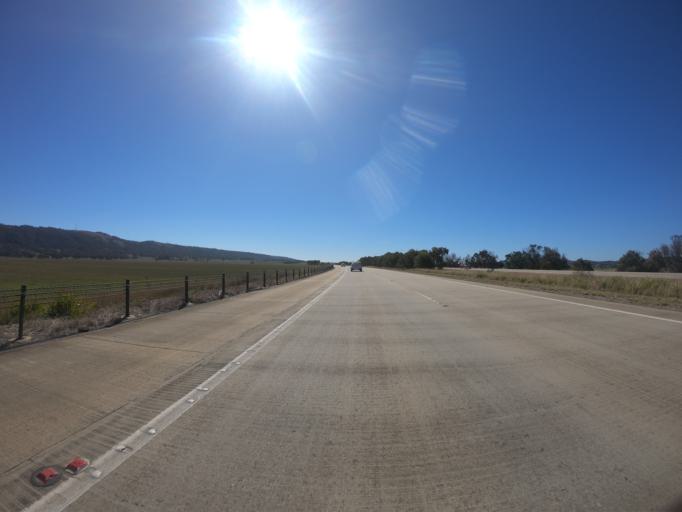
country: AU
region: New South Wales
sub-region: Yass Valley
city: Gundaroo
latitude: -34.9602
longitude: 149.4073
